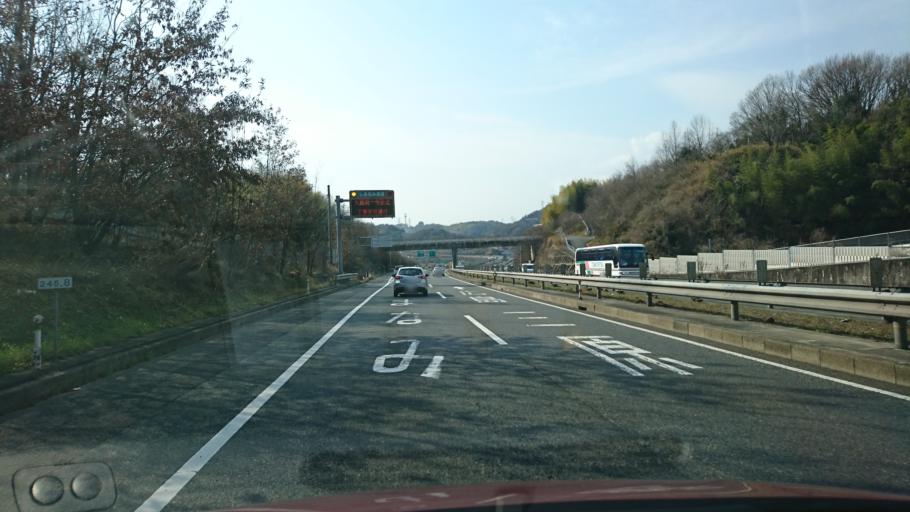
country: JP
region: Hiroshima
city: Onomichi
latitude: 34.4359
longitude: 133.2238
